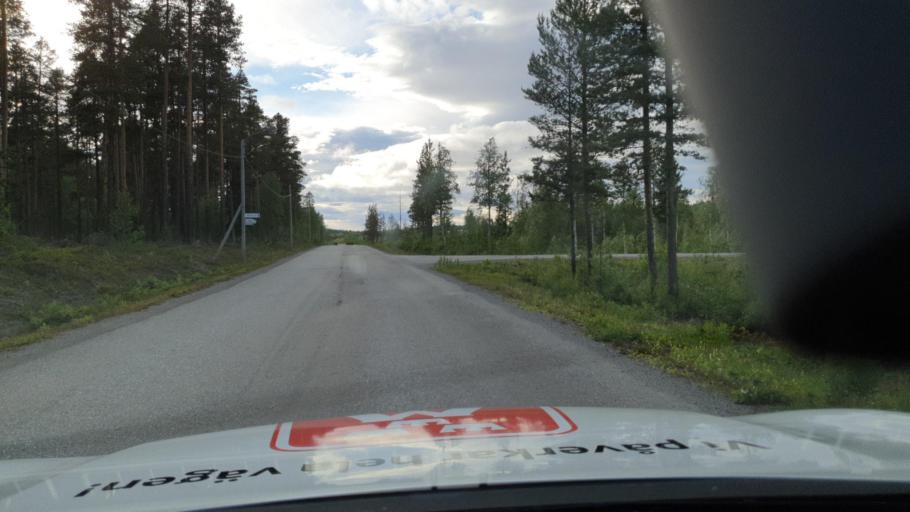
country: SE
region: Vaesterbotten
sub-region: Storumans Kommun
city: Storuman
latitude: 65.0722
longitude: 17.1236
